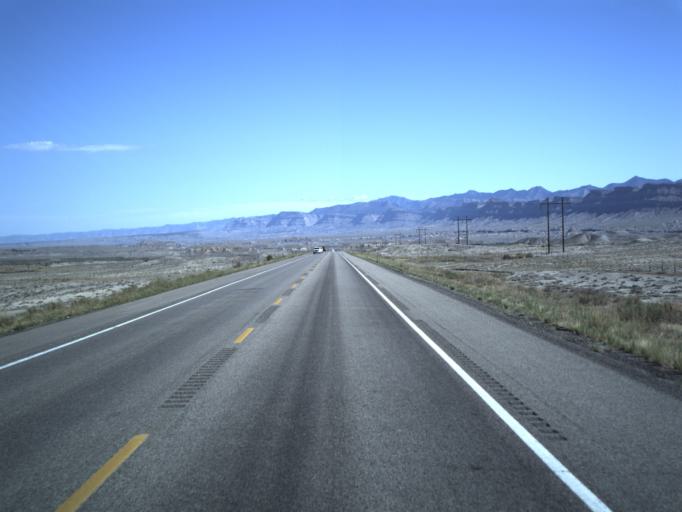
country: US
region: Utah
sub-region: Carbon County
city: East Carbon City
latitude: 39.2153
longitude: -110.3386
